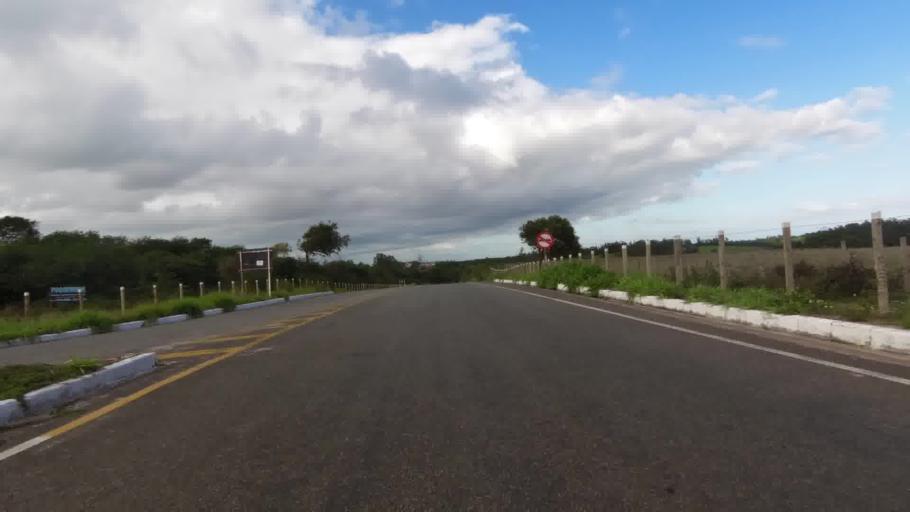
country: BR
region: Espirito Santo
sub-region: Piuma
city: Piuma
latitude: -20.7899
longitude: -40.6029
